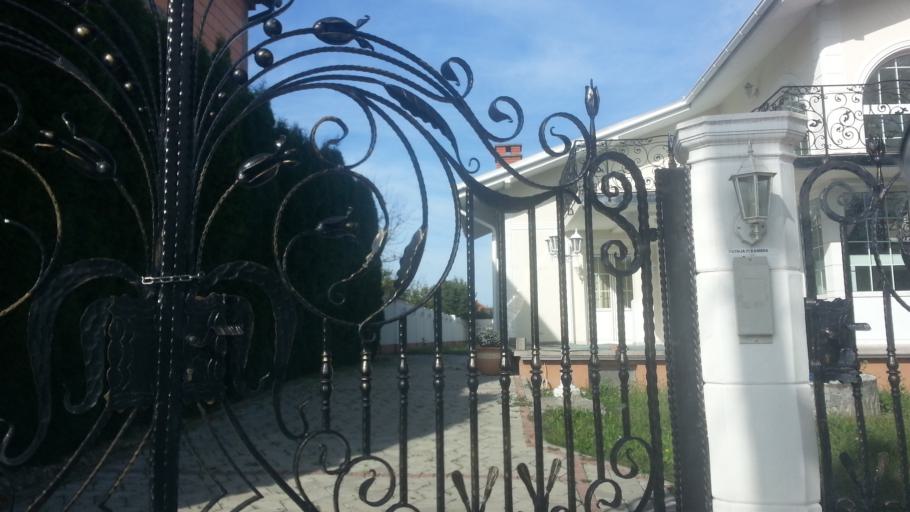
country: RS
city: Novi Banovci
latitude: 44.9614
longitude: 20.2826
